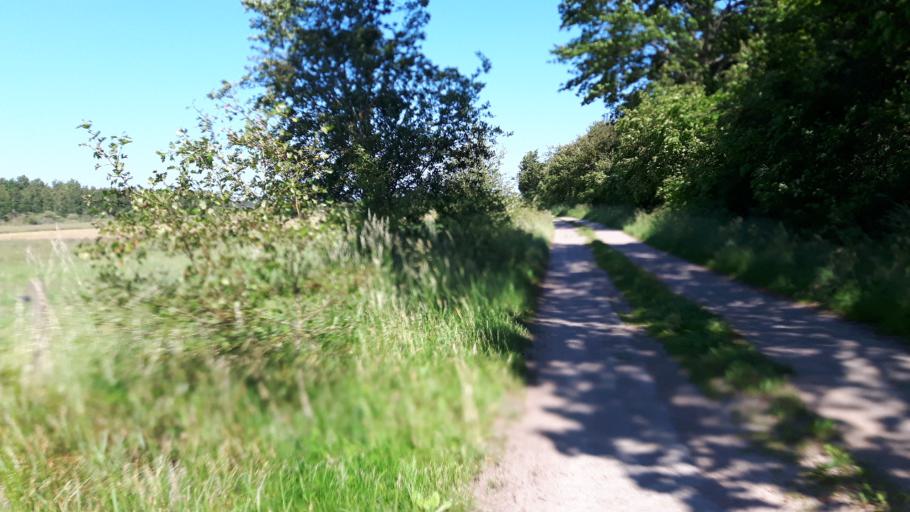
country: PL
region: Pomeranian Voivodeship
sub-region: Powiat slupski
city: Glowczyce
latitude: 54.6415
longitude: 17.3891
